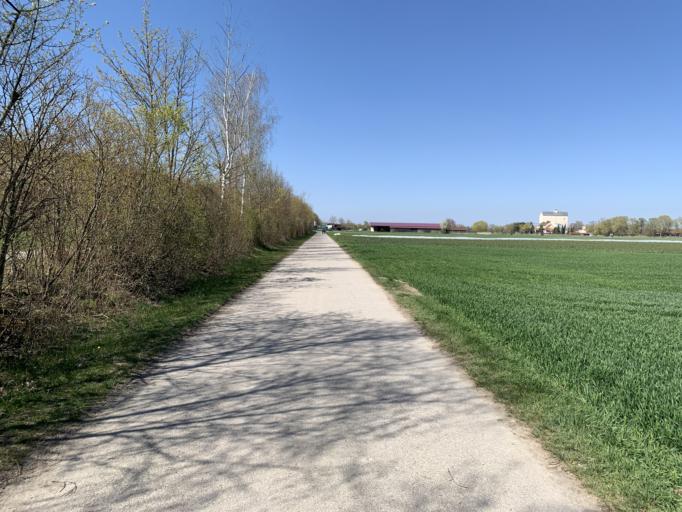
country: DE
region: Bavaria
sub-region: Swabia
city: Gersthofen
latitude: 48.4168
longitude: 10.8994
